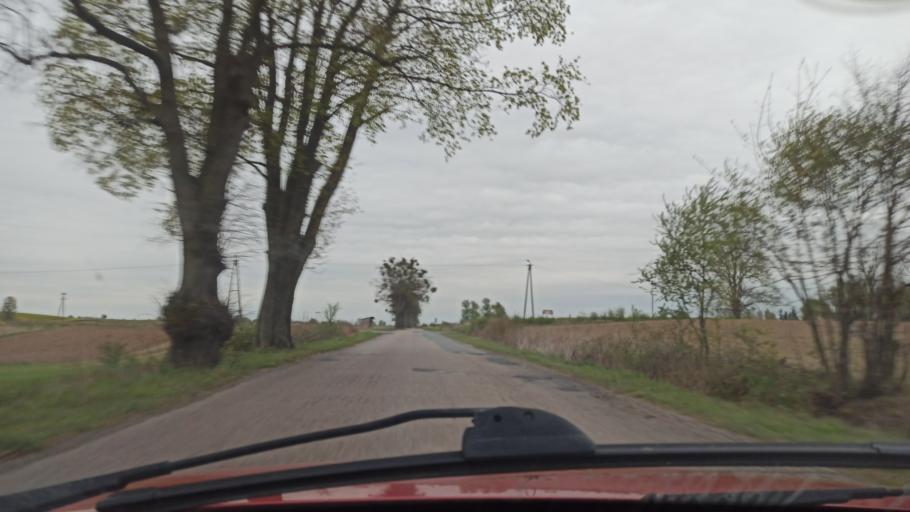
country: PL
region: Pomeranian Voivodeship
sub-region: Powiat kwidzynski
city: Gardeja
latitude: 53.5700
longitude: 18.9951
